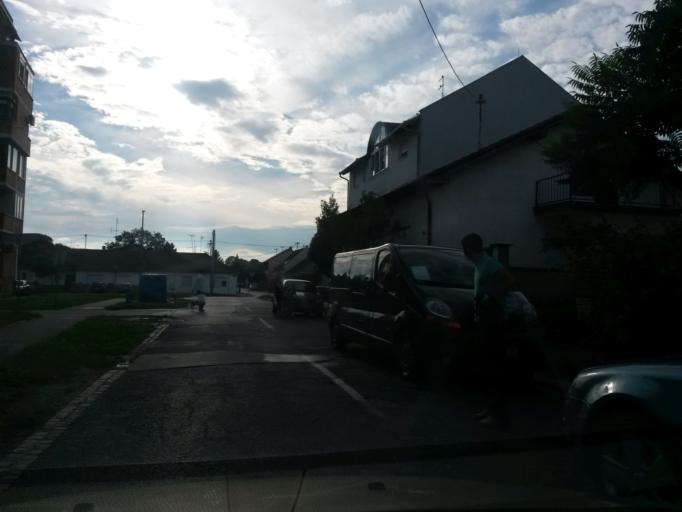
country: HR
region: Osjecko-Baranjska
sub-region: Grad Osijek
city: Osijek
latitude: 45.5499
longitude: 18.7100
